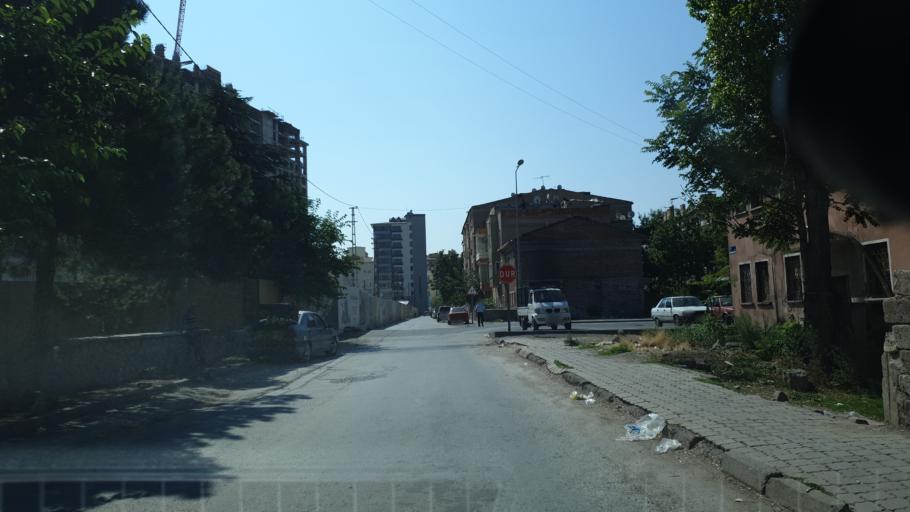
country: TR
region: Kayseri
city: Kayseri
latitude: 38.7287
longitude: 35.4893
